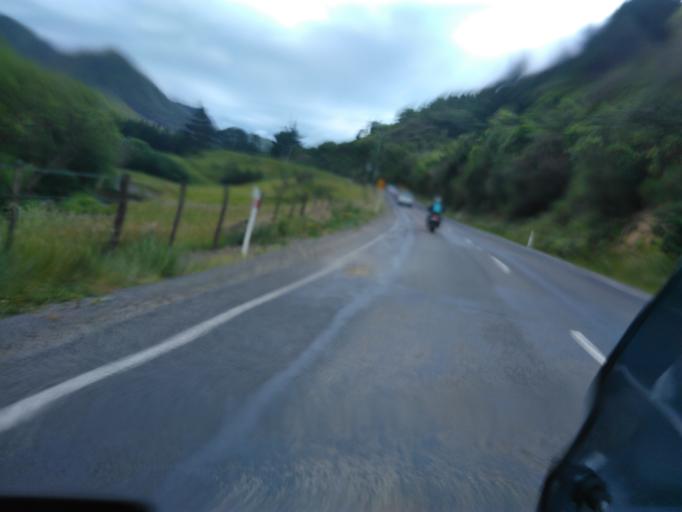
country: NZ
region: Bay of Plenty
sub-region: Opotiki District
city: Opotiki
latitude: -38.3731
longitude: 177.4874
